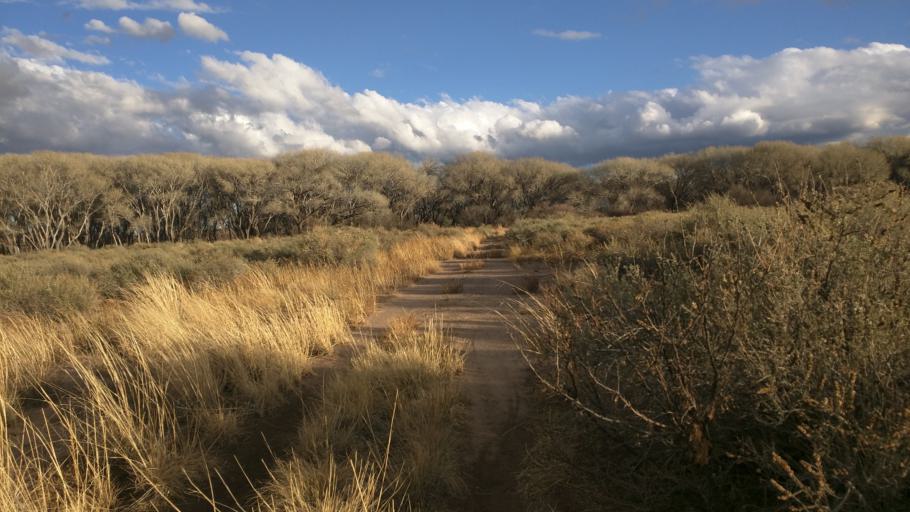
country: US
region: Arizona
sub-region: Cochise County
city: Sierra Vista Southeast
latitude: 31.3686
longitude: -110.1210
